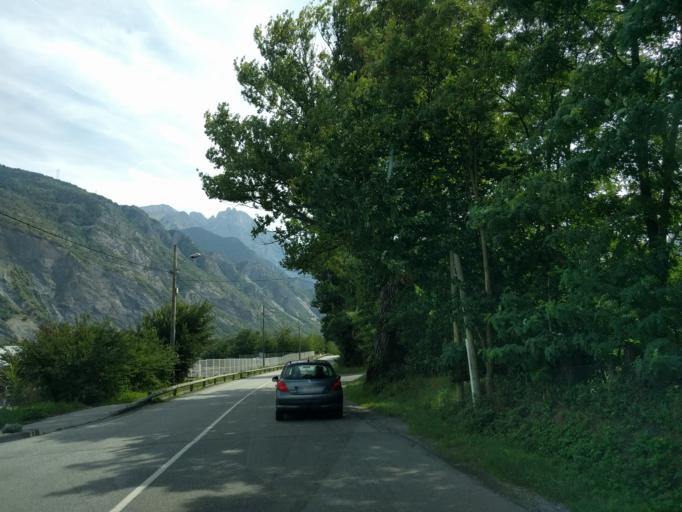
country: FR
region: Rhone-Alpes
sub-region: Departement de la Savoie
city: Villargondran
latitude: 45.2701
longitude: 6.3598
